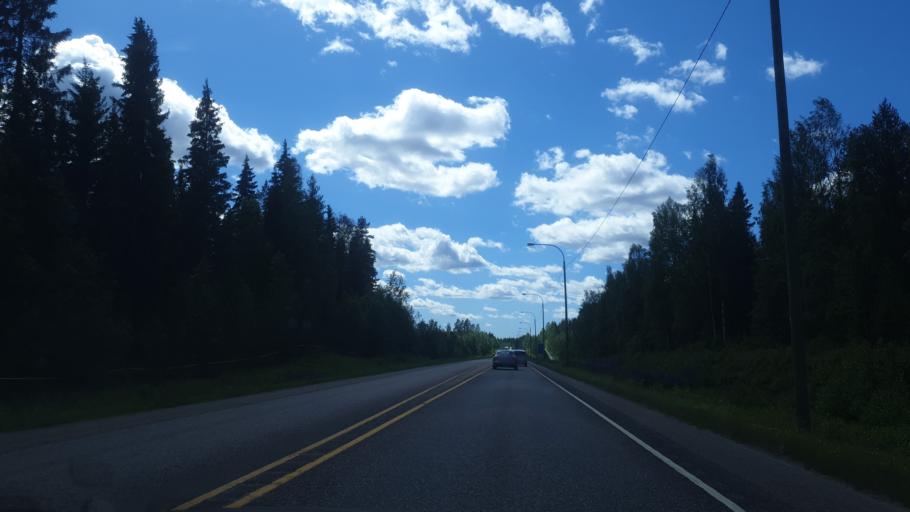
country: FI
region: Northern Savo
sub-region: Varkaus
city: Varkaus
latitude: 62.3967
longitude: 27.8201
